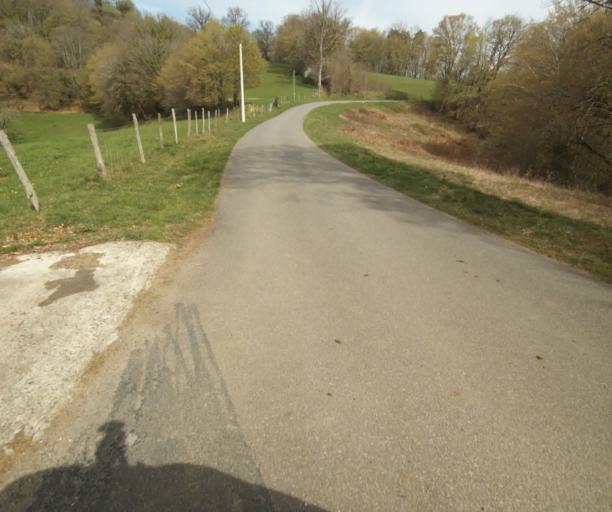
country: FR
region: Limousin
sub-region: Departement de la Correze
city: Naves
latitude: 45.3306
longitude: 1.8027
